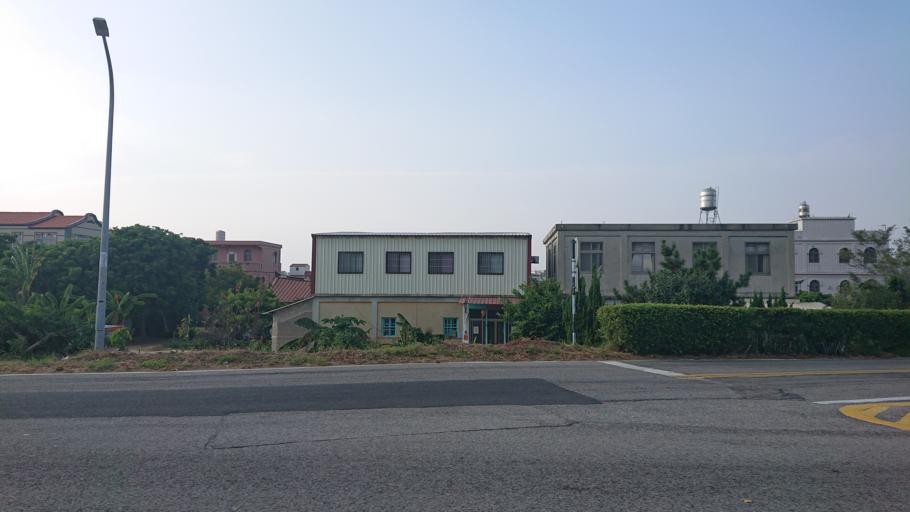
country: TW
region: Fukien
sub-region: Kinmen
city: Jincheng
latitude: 24.4791
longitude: 118.4291
